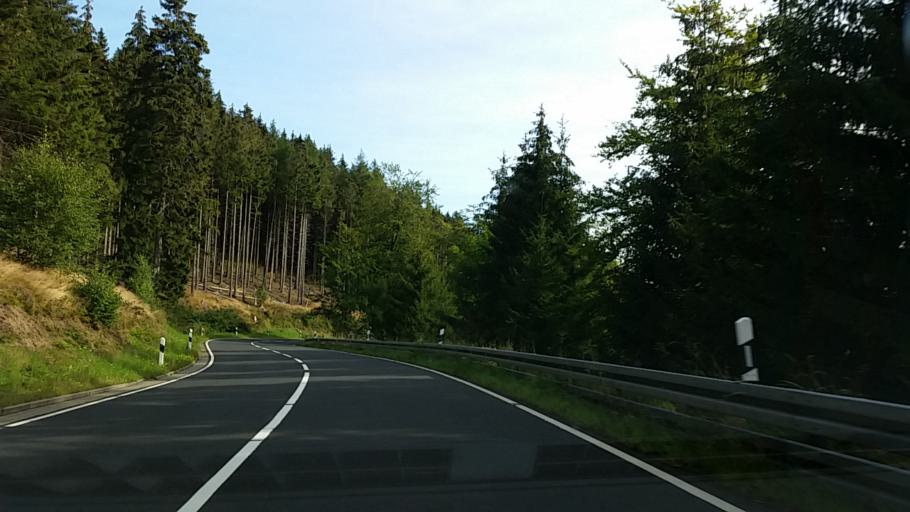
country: DE
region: Lower Saxony
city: Goslar
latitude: 51.8679
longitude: 10.3827
